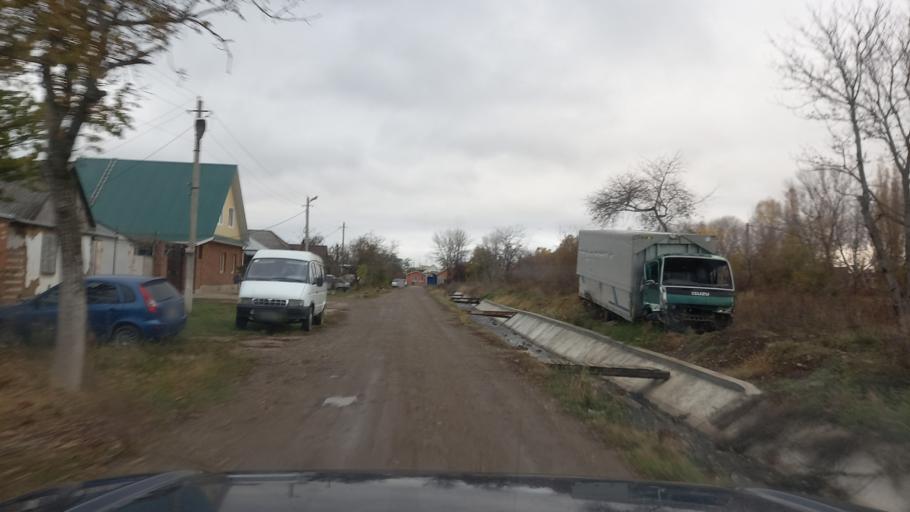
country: RU
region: Adygeya
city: Maykop
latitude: 44.6203
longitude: 40.1289
